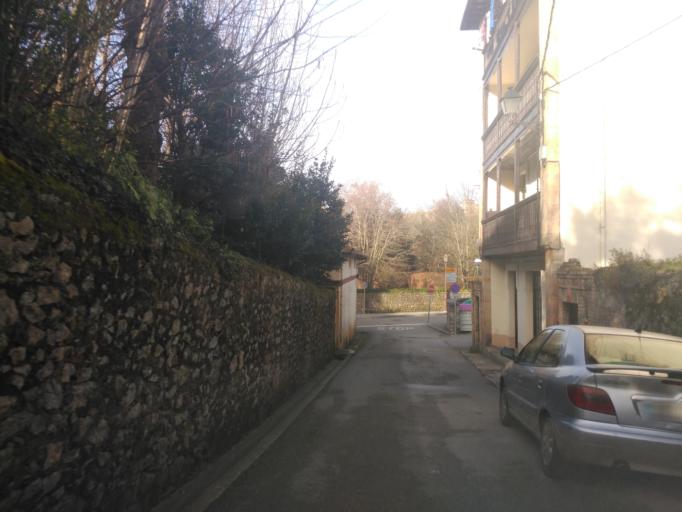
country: ES
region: Cantabria
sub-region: Provincia de Cantabria
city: Comillas
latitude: 43.3847
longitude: -4.2910
